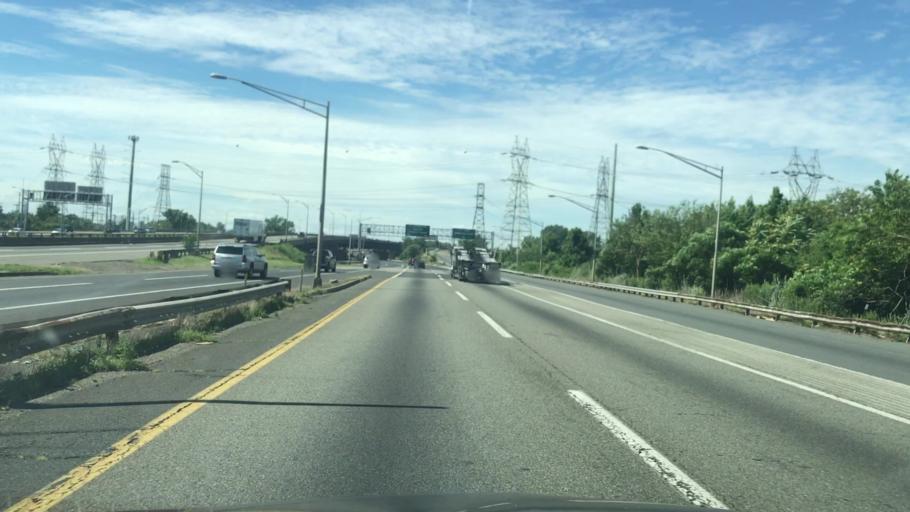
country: US
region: New Jersey
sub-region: Bergen County
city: Ridgefield
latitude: 40.8374
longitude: -74.0201
